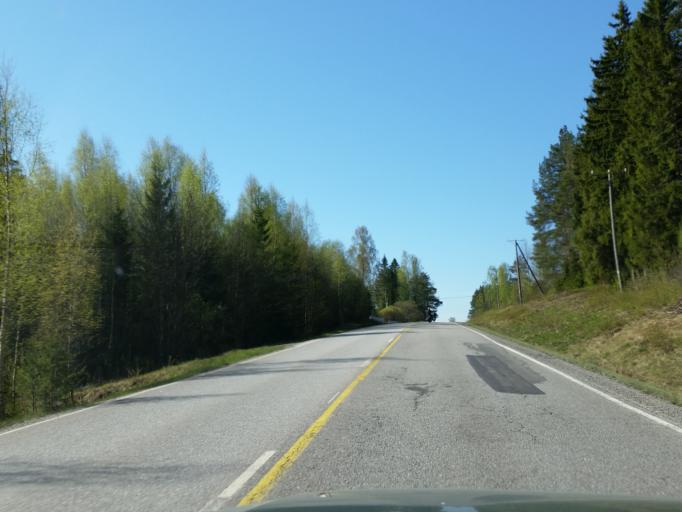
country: FI
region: Uusimaa
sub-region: Helsinki
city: Siuntio
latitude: 60.1904
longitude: 24.2474
